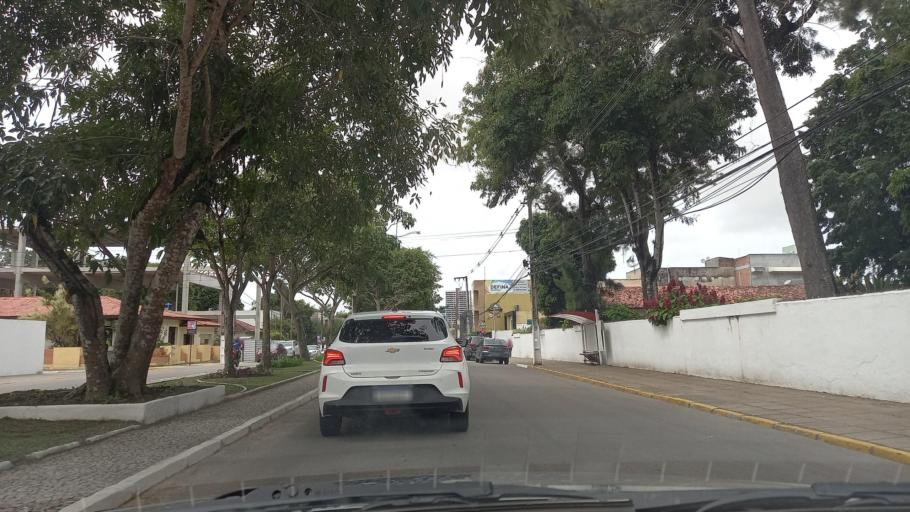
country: BR
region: Pernambuco
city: Garanhuns
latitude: -8.8858
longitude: -36.4846
